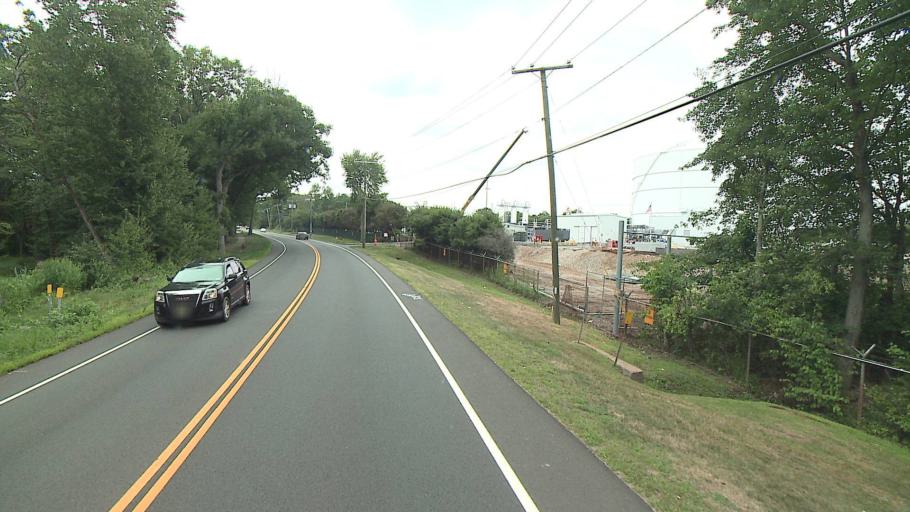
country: US
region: Connecticut
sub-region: Middlesex County
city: Cromwell
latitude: 41.6342
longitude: -72.6755
